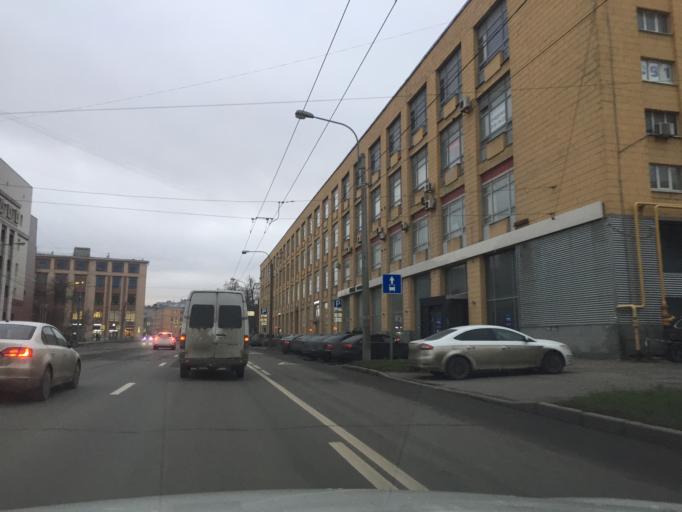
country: RU
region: St.-Petersburg
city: Petrogradka
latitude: 59.9726
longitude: 30.3153
